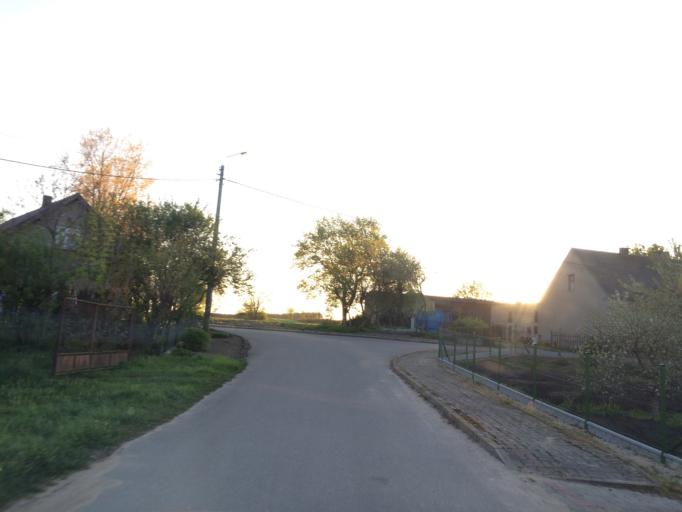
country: PL
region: Warmian-Masurian Voivodeship
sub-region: Powiat dzialdowski
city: Rybno
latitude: 53.4462
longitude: 19.9036
